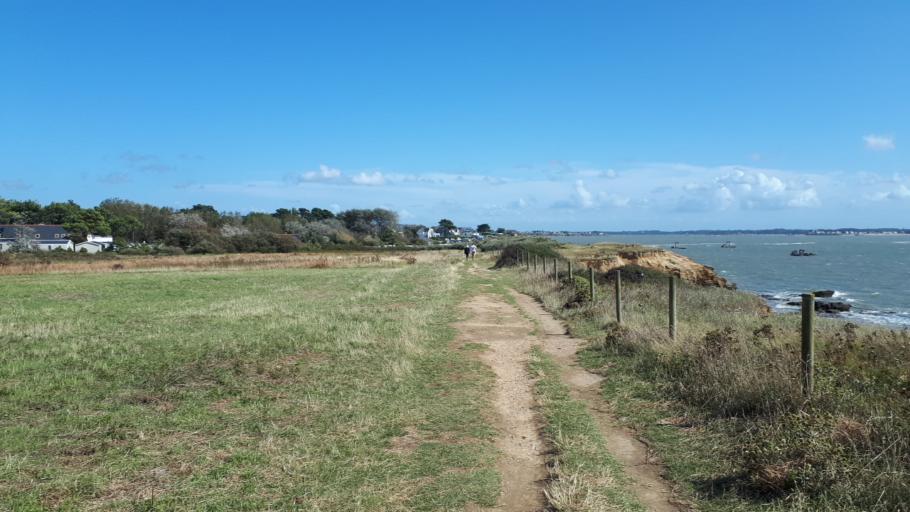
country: FR
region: Brittany
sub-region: Departement du Morbihan
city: Penestin
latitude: 47.4454
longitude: -2.4867
